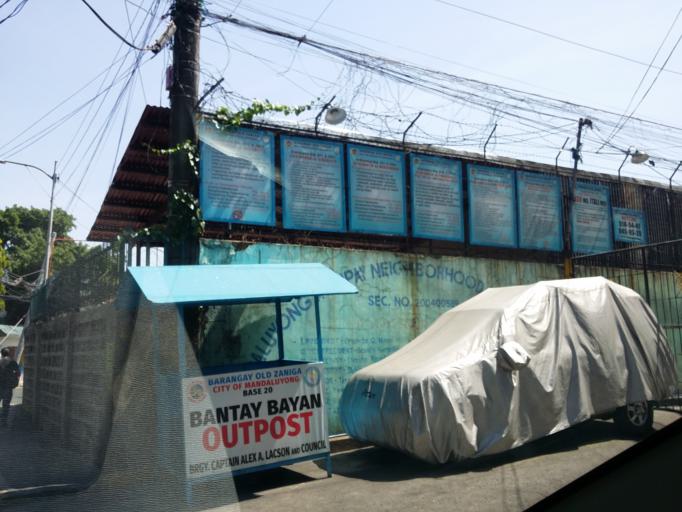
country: PH
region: Metro Manila
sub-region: Mandaluyong
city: Mandaluyong City
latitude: 14.5834
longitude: 121.0247
